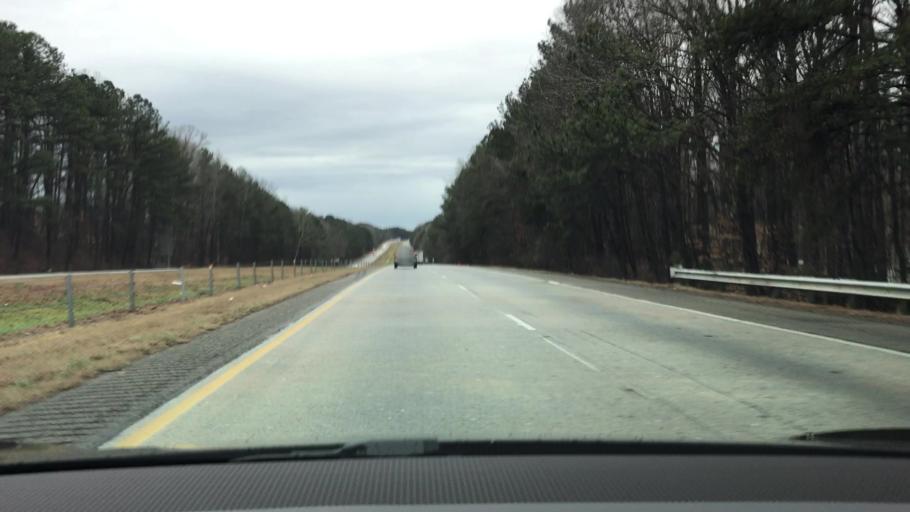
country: US
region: Georgia
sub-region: Gwinnett County
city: Buford
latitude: 34.0793
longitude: -83.9989
